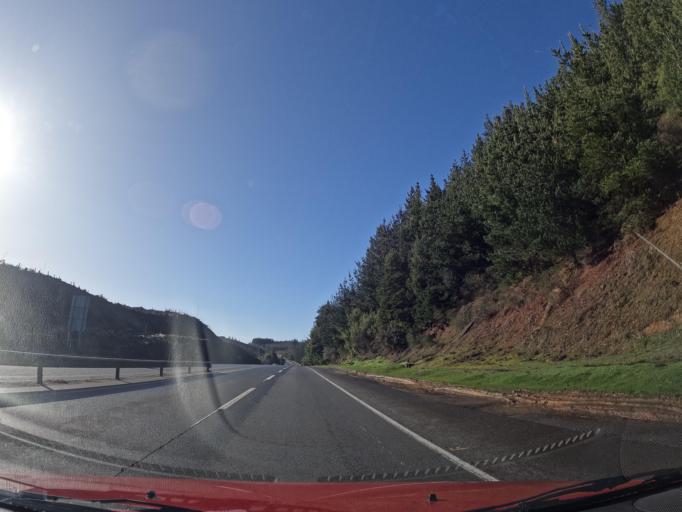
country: CL
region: Biobio
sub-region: Provincia de Concepcion
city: Penco
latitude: -36.7594
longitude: -72.9485
